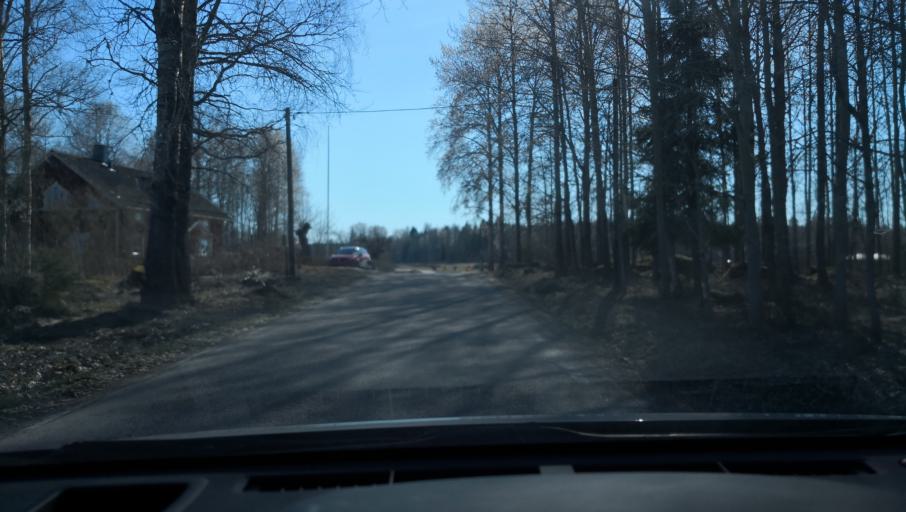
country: SE
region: Vaestmanland
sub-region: Sala Kommun
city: Sala
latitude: 60.0844
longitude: 16.5010
